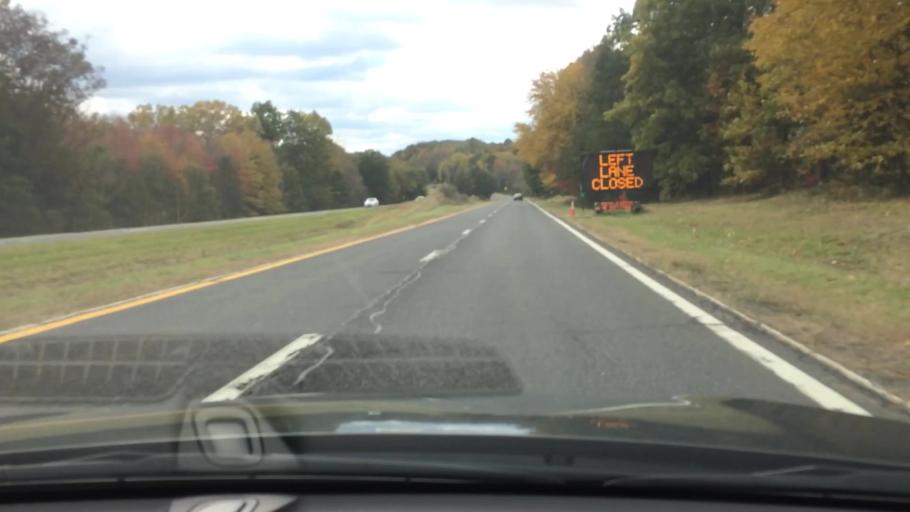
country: US
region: New York
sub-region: Dutchess County
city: Pleasant Valley
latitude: 41.7099
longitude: -73.7826
